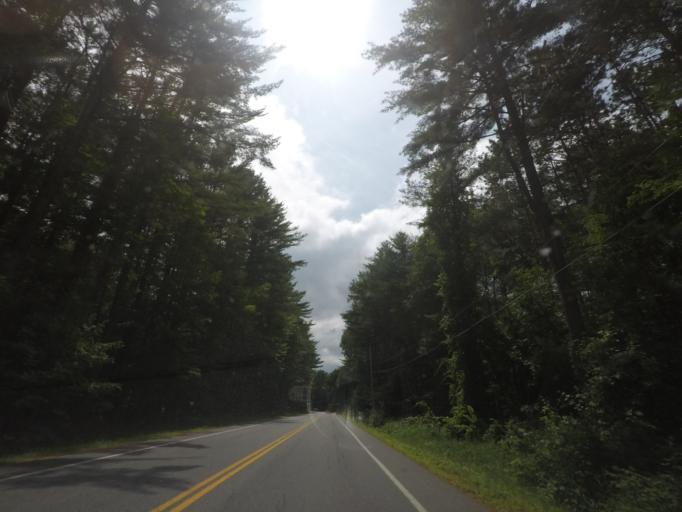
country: US
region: New York
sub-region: Saratoga County
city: Saratoga Springs
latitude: 43.0743
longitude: -73.7071
